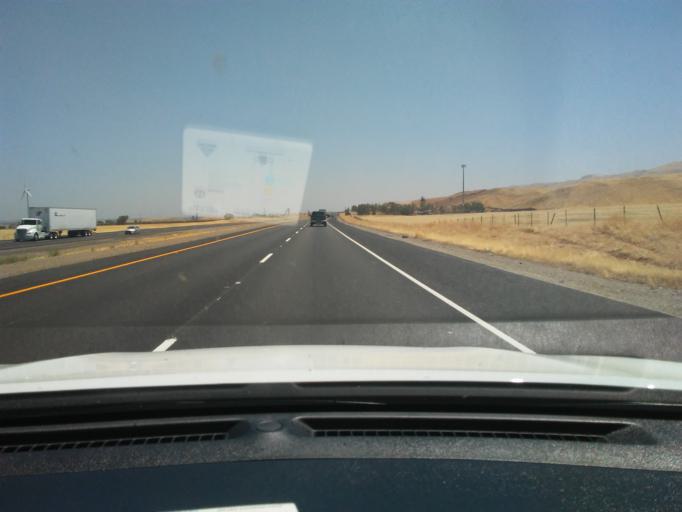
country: US
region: California
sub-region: San Joaquin County
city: Tracy
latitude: 37.6235
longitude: -121.3760
